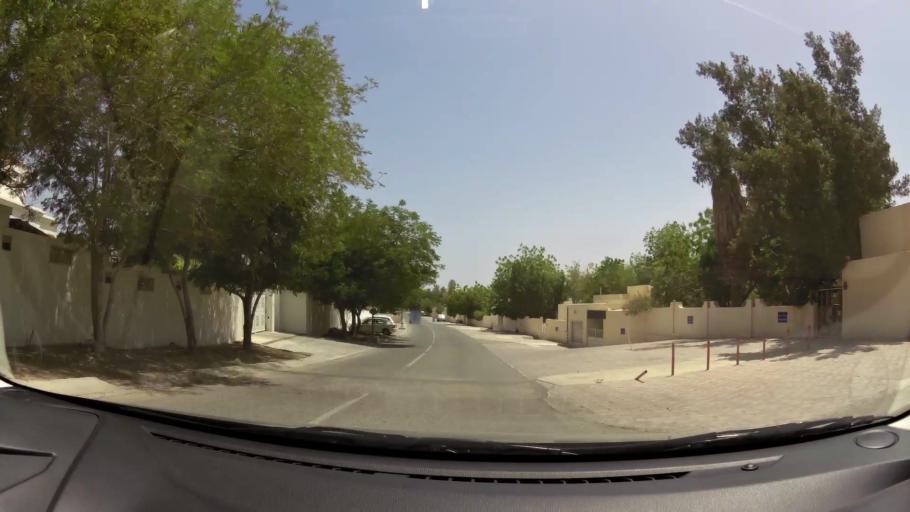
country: OM
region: Muhafazat Masqat
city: Bawshar
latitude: 23.5871
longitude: 58.4509
